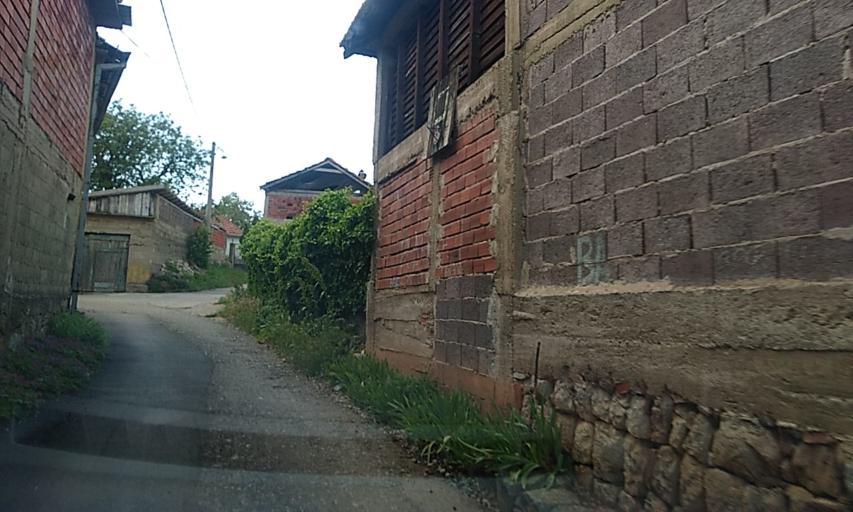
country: RS
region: Central Serbia
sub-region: Nisavski Okrug
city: Niska Banja
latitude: 43.3675
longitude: 21.9988
